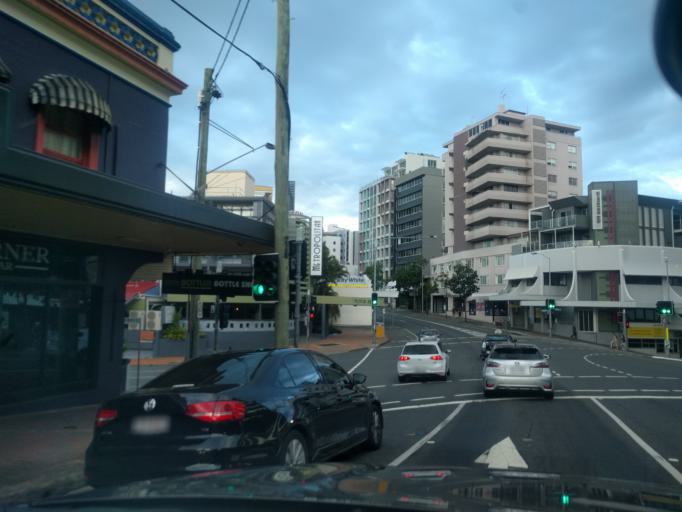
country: AU
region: Queensland
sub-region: Brisbane
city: Spring Hill
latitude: -27.4626
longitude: 153.0239
